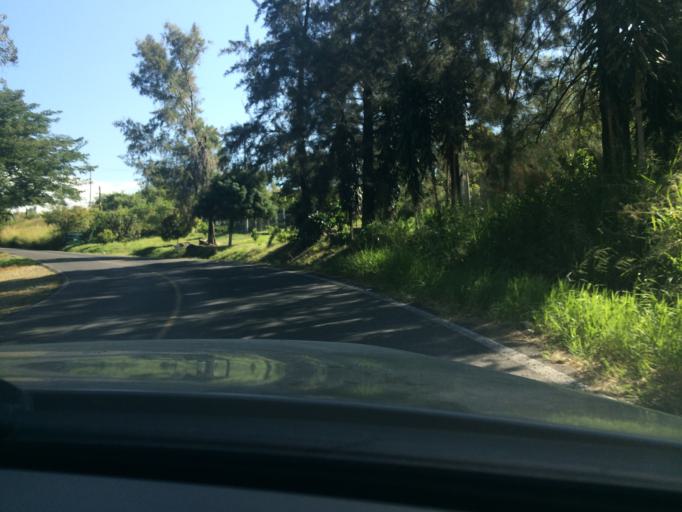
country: MX
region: Colima
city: Suchitlan
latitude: 19.3734
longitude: -103.7206
